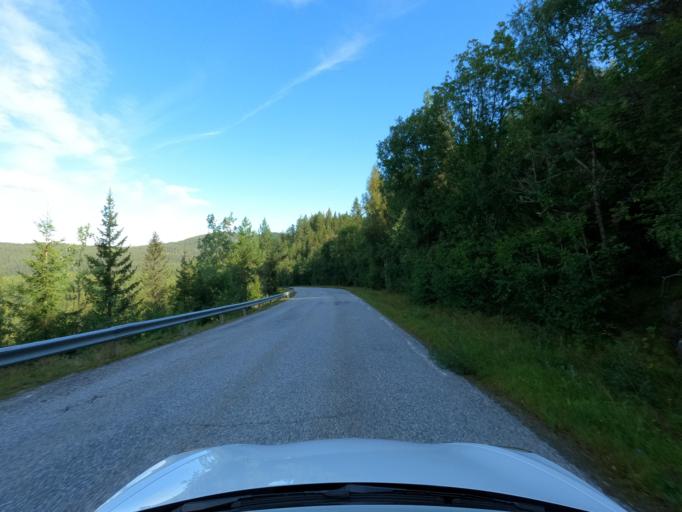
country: NO
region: Telemark
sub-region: Hjartdal
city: Sauland
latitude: 59.9183
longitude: 8.9800
